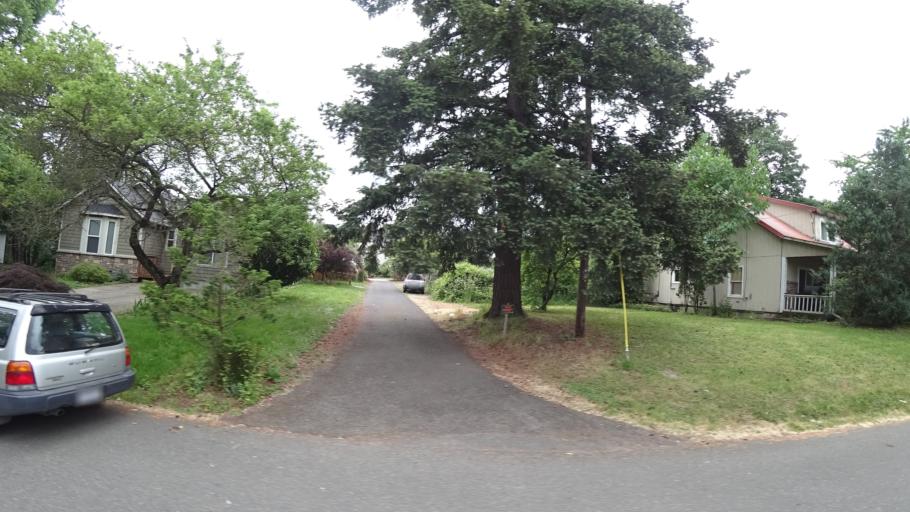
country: US
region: Oregon
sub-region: Multnomah County
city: Lents
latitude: 45.4996
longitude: -122.5701
